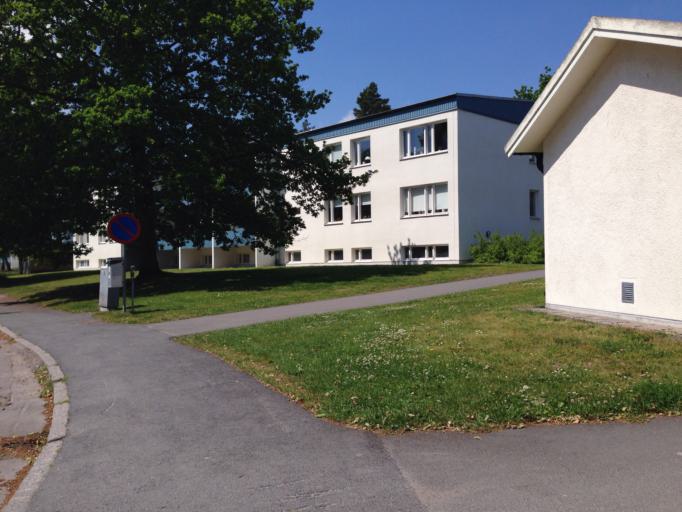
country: SE
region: Kalmar
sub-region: Kalmar Kommun
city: Kalmar
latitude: 56.6551
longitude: 16.3315
